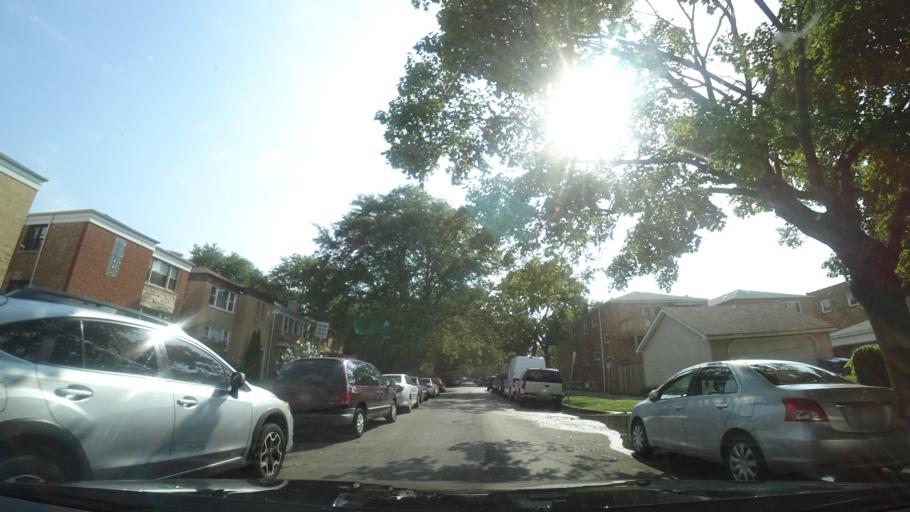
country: US
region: Illinois
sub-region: Cook County
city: Evanston
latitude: 42.0105
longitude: -87.6961
